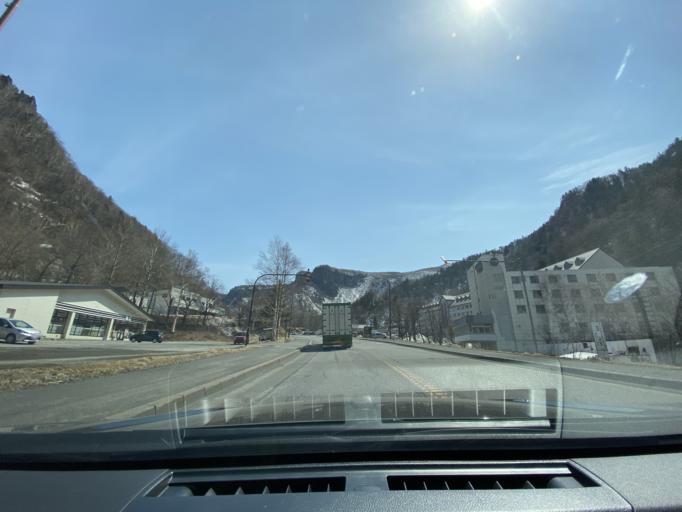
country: JP
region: Hokkaido
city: Kamikawa
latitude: 43.7308
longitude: 142.9423
